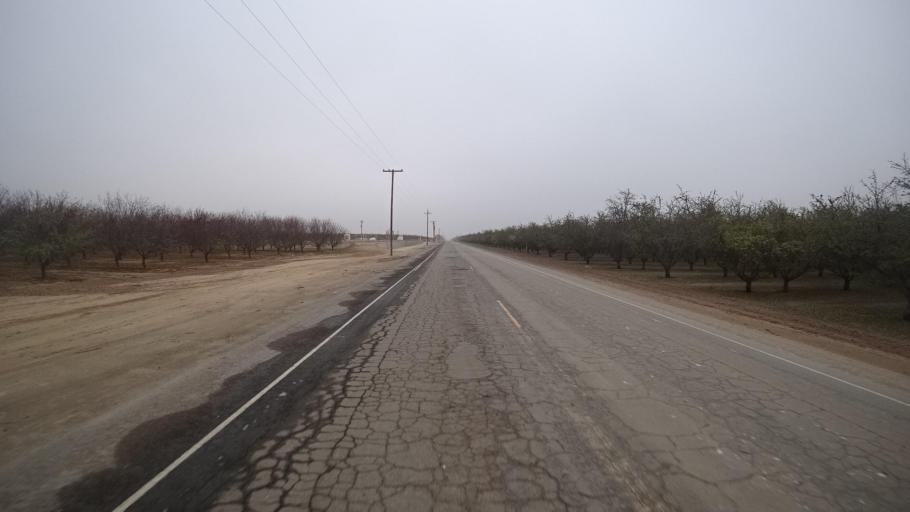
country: US
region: California
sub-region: Kern County
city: Wasco
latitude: 35.5576
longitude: -119.4894
